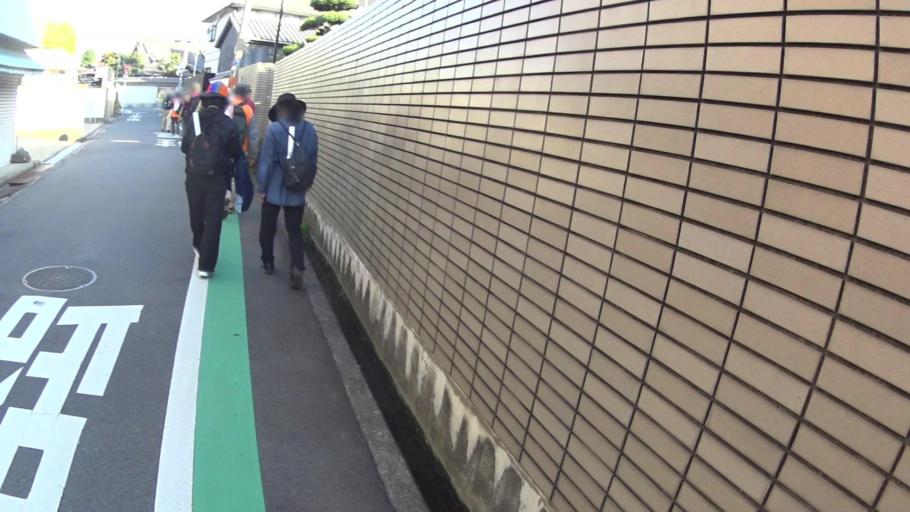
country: JP
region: Osaka
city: Kashihara
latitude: 34.5794
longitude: 135.5937
